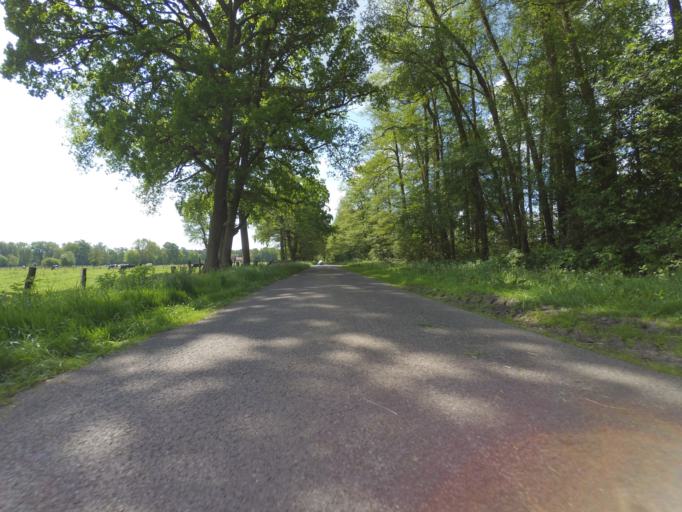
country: DE
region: Lower Saxony
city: Isernhagen Farster Bauerschaft
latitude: 52.5299
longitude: 9.9193
